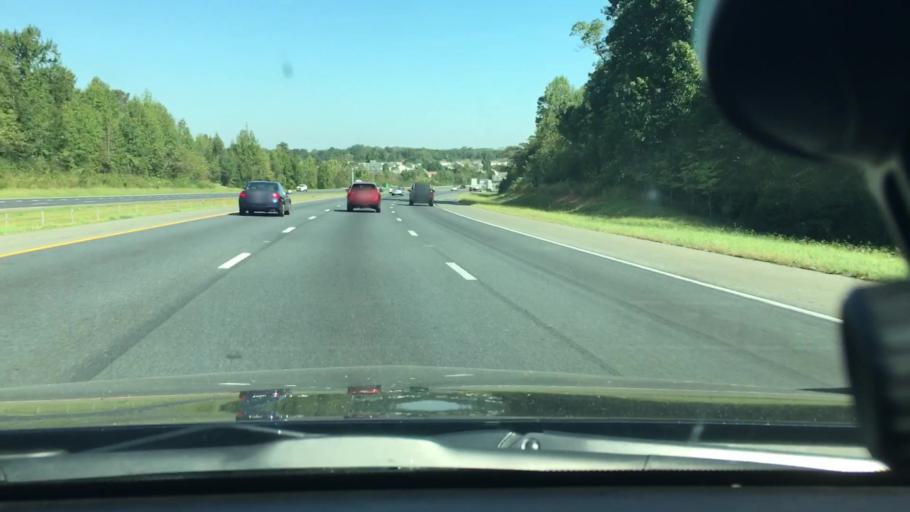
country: US
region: North Carolina
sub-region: Mecklenburg County
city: Mint Hill
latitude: 35.2288
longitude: -80.6542
